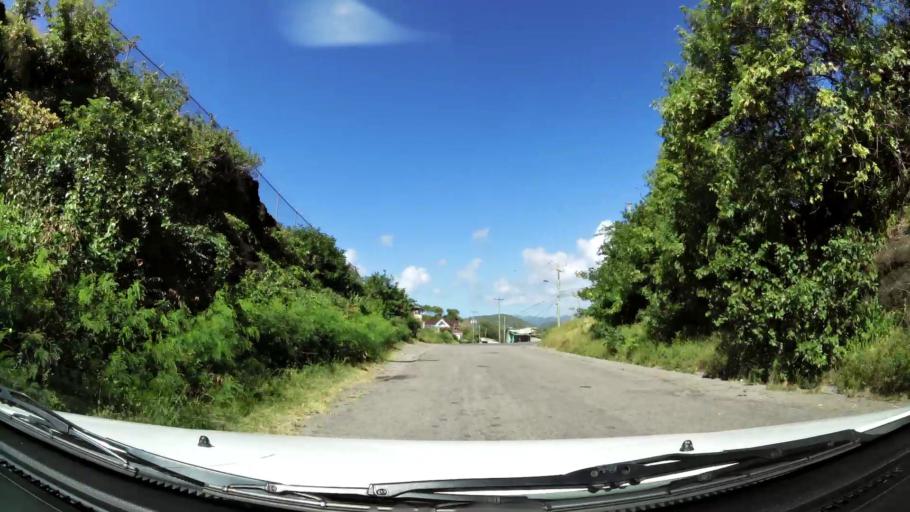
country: LC
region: Vieux-Fort
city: Vieux Fort
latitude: 13.7240
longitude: -60.9522
